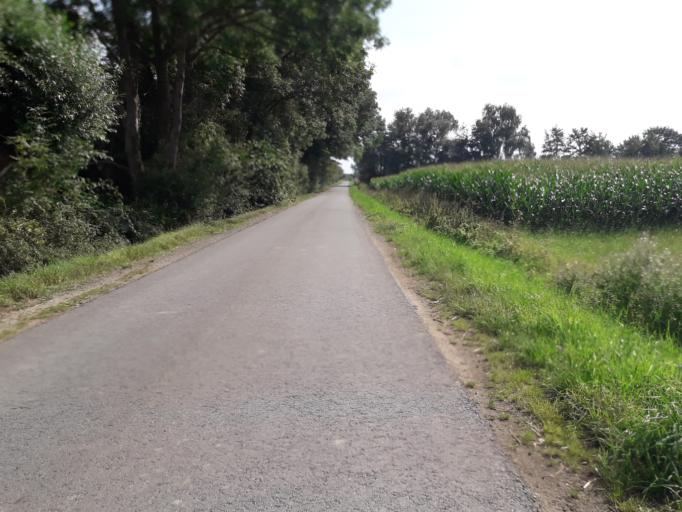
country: DE
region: North Rhine-Westphalia
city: Bad Lippspringe
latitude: 51.7611
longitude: 8.8034
